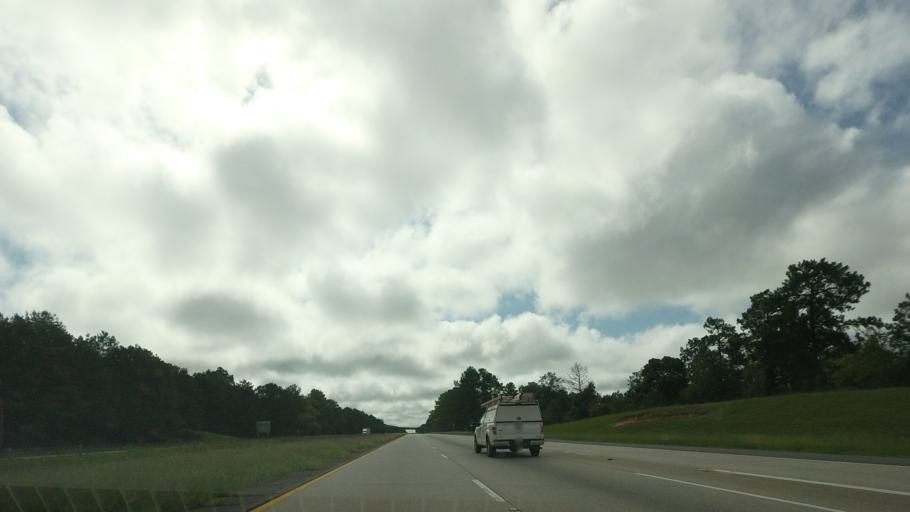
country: US
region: Georgia
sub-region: Houston County
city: Warner Robins
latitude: 32.7174
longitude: -83.5284
